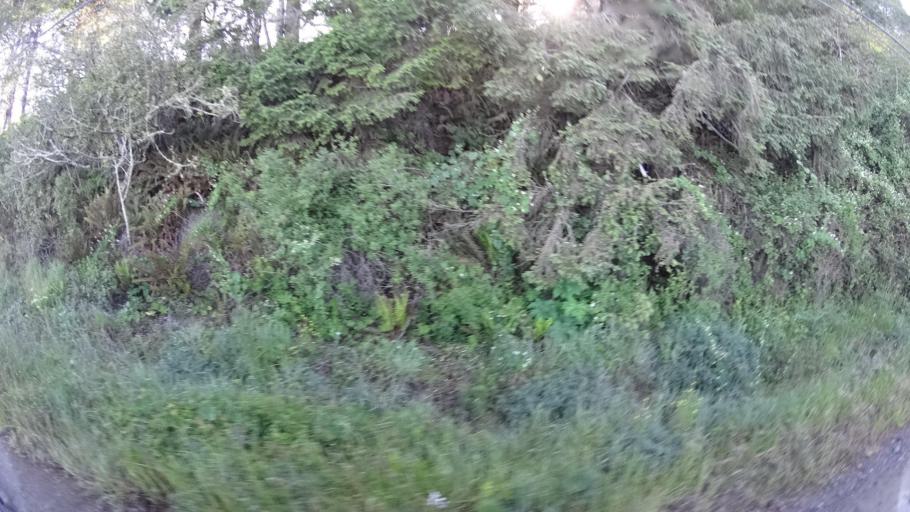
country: US
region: California
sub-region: Humboldt County
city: Westhaven-Moonstone
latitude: 41.1077
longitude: -124.1598
